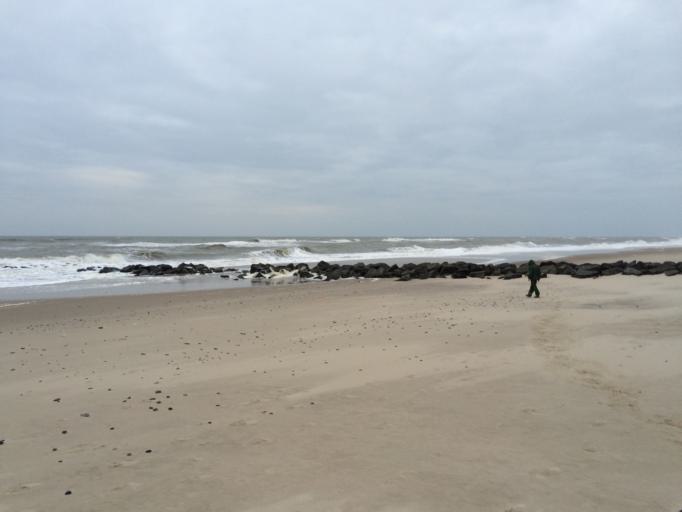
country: DK
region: Central Jutland
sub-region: Holstebro Kommune
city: Ulfborg
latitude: 56.3778
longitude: 8.1170
